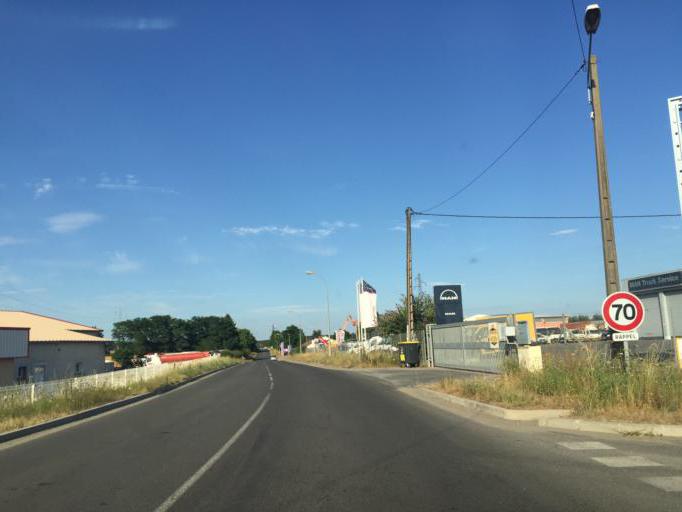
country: FR
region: Auvergne
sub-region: Departement de l'Allier
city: Toulon-sur-Allier
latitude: 46.5371
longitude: 3.3612
